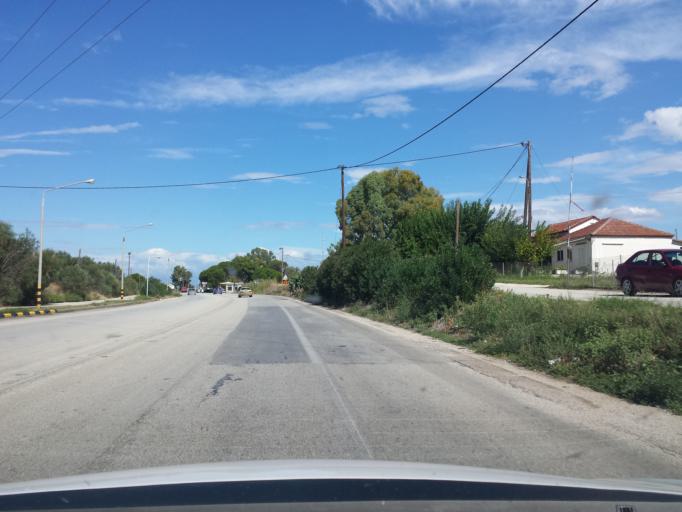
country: GR
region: West Greece
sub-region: Nomos Achaias
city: Kato Achaia
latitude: 38.1310
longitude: 21.5481
